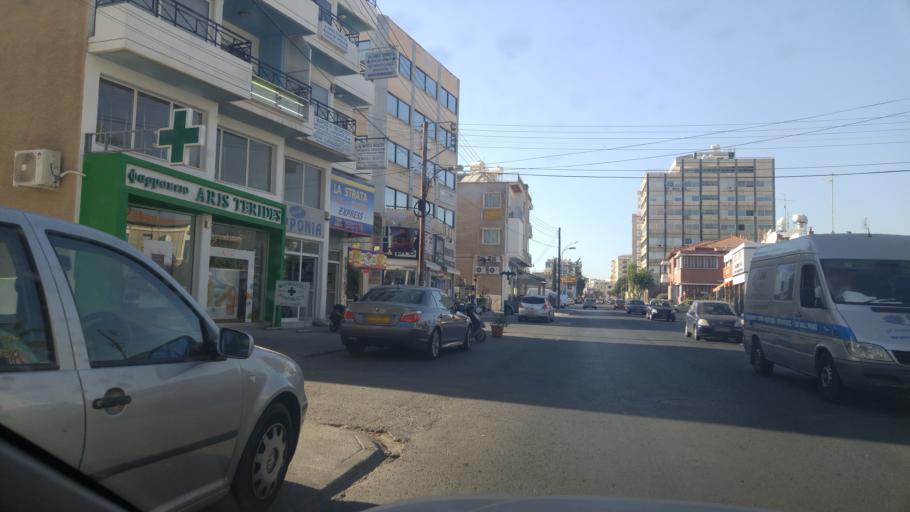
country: CY
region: Limassol
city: Limassol
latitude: 34.6821
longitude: 33.0324
